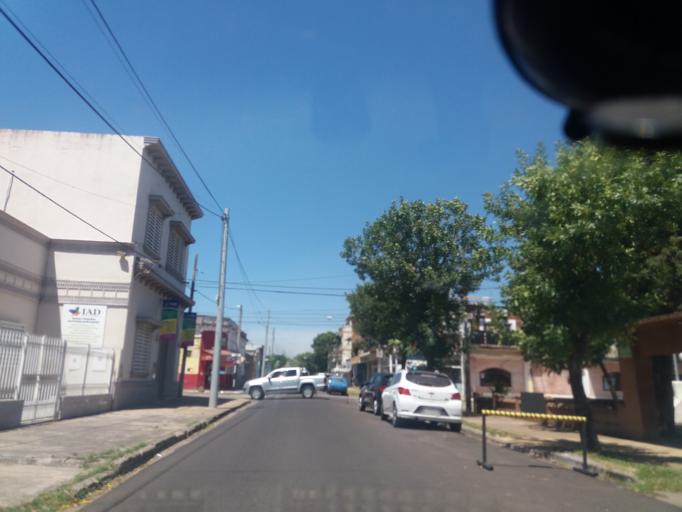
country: AR
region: Corrientes
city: Corrientes
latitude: -27.4804
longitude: -58.8451
